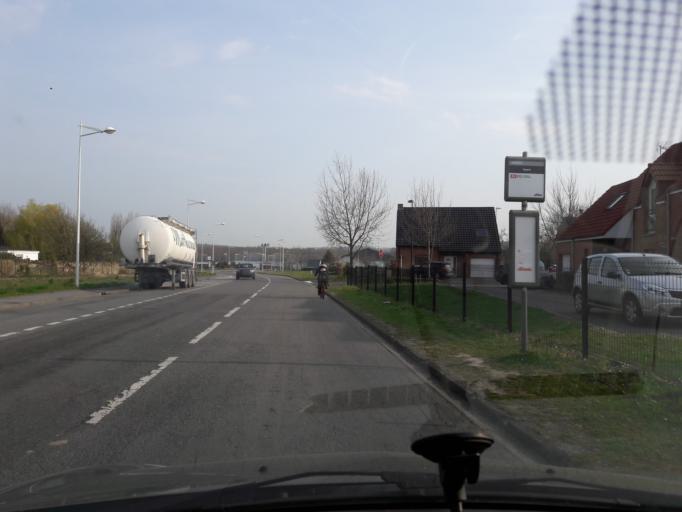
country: FR
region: Nord-Pas-de-Calais
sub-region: Departement du Nord
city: Recquignies
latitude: 50.2874
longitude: 4.0265
